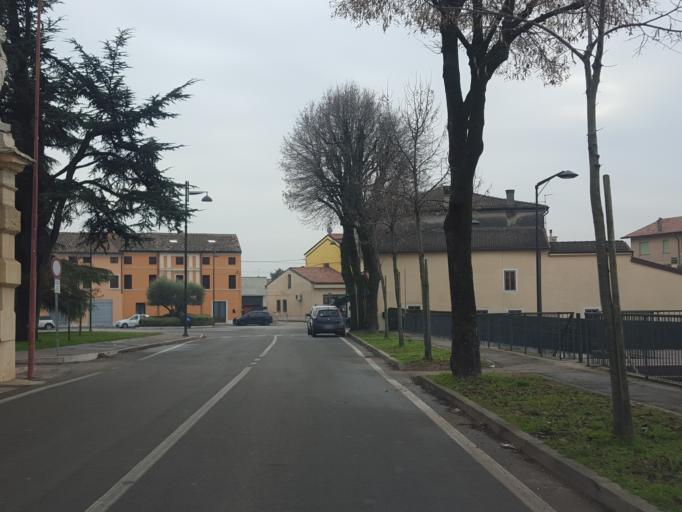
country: IT
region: Veneto
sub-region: Provincia di Verona
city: Arcole
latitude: 45.3593
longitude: 11.2845
